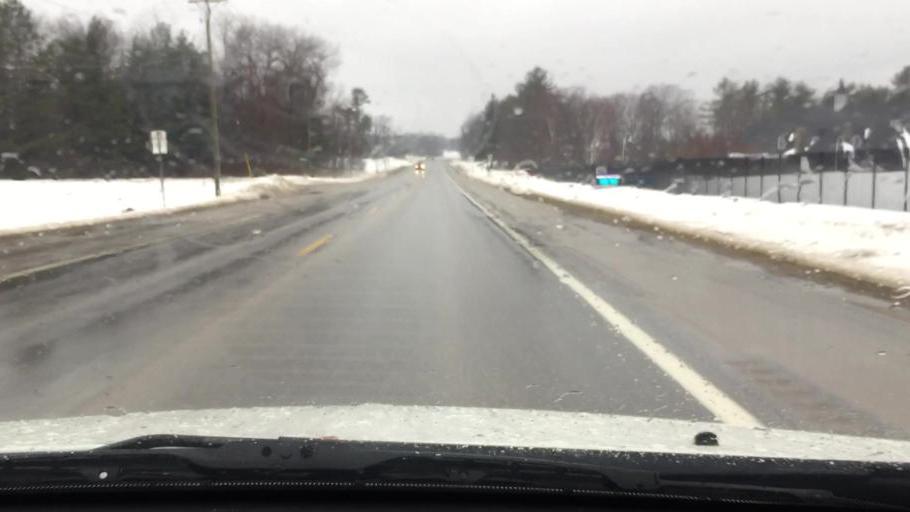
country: US
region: Michigan
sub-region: Charlevoix County
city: Charlevoix
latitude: 45.2792
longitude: -85.2305
